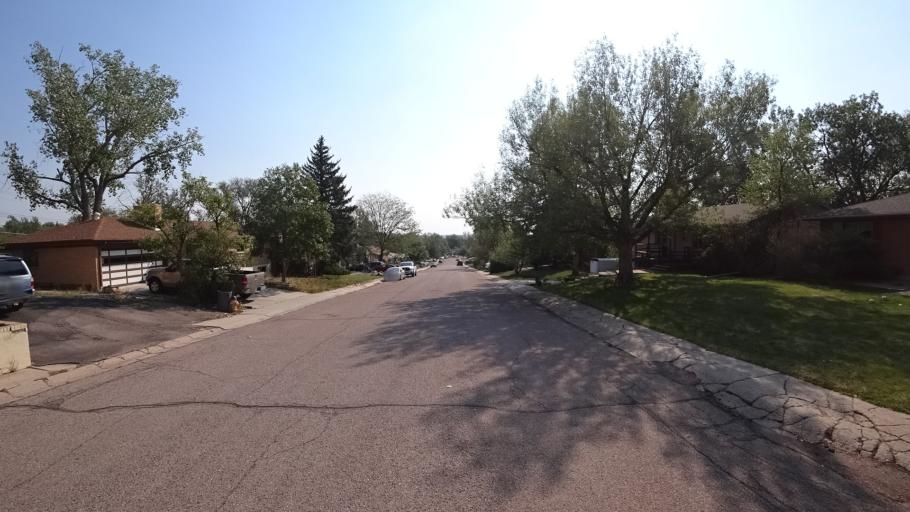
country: US
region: Colorado
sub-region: El Paso County
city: Colorado Springs
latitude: 38.8098
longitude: -104.8395
